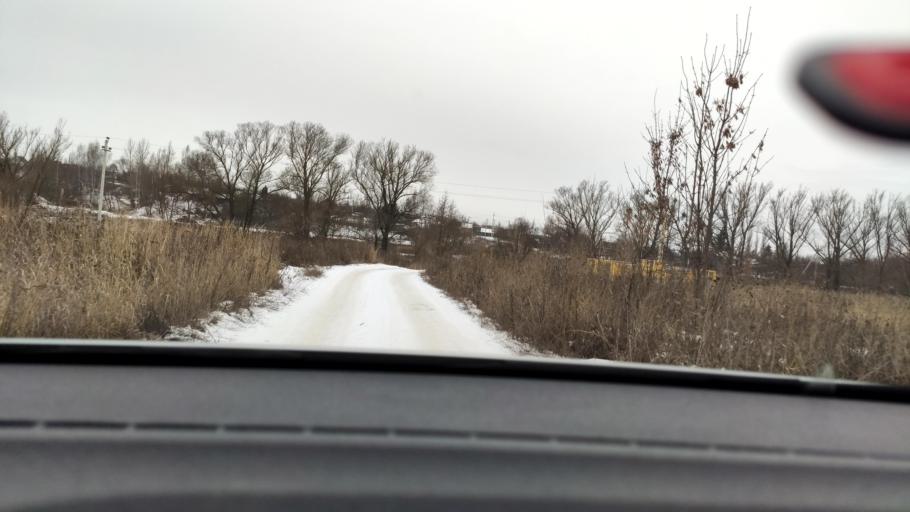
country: RU
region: Voronezj
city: Semiluki
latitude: 51.7007
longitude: 38.9973
